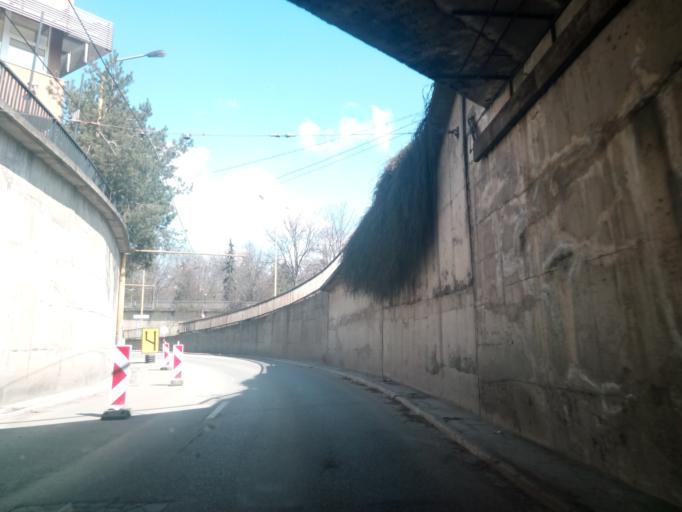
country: SK
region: Kosicky
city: Kosice
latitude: 48.7207
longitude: 21.2641
